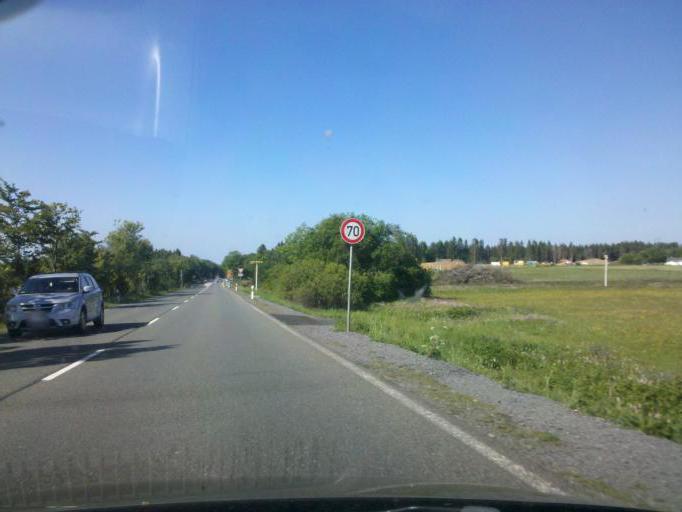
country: DE
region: Rheinland-Pfalz
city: Liebenscheid
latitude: 50.7131
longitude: 8.0698
